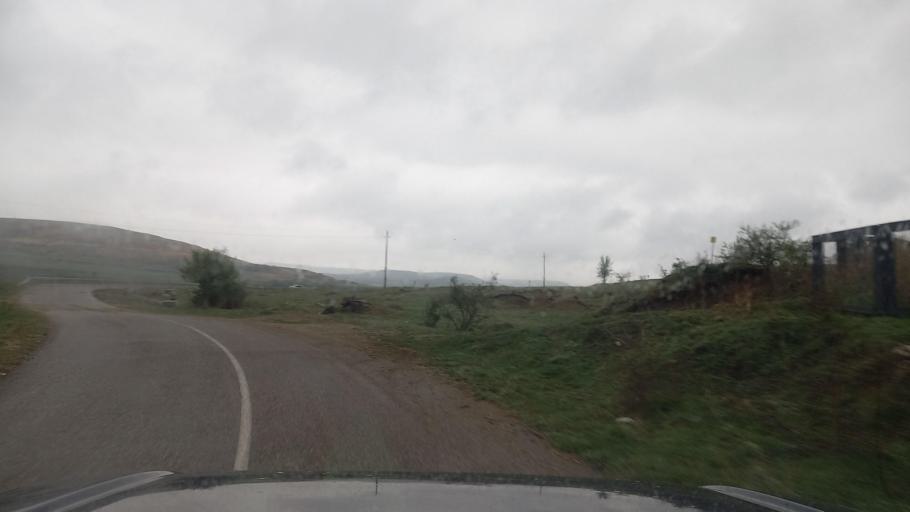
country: RU
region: Stavropol'skiy
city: Nezhinskiy
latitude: 43.8648
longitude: 42.6620
